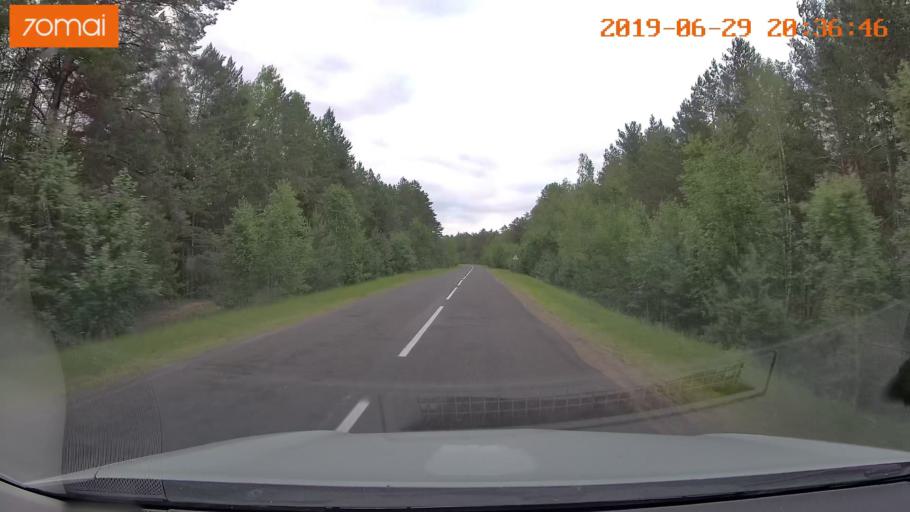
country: BY
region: Brest
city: Hantsavichy
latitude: 52.5300
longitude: 26.3612
